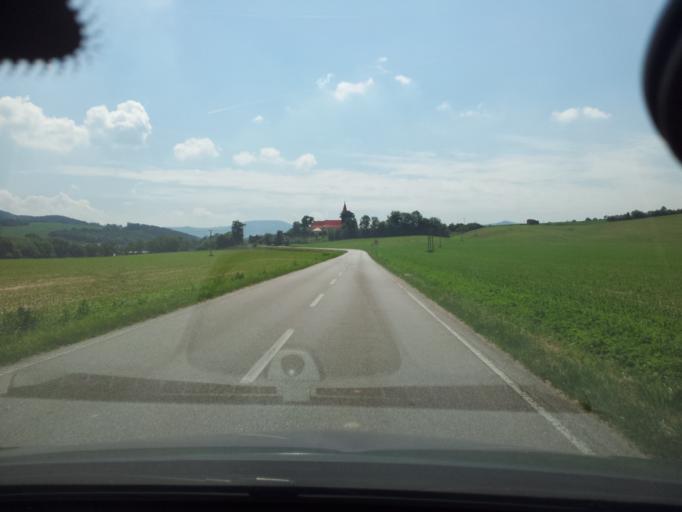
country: SK
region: Nitriansky
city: Partizanske
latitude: 48.6203
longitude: 18.4298
